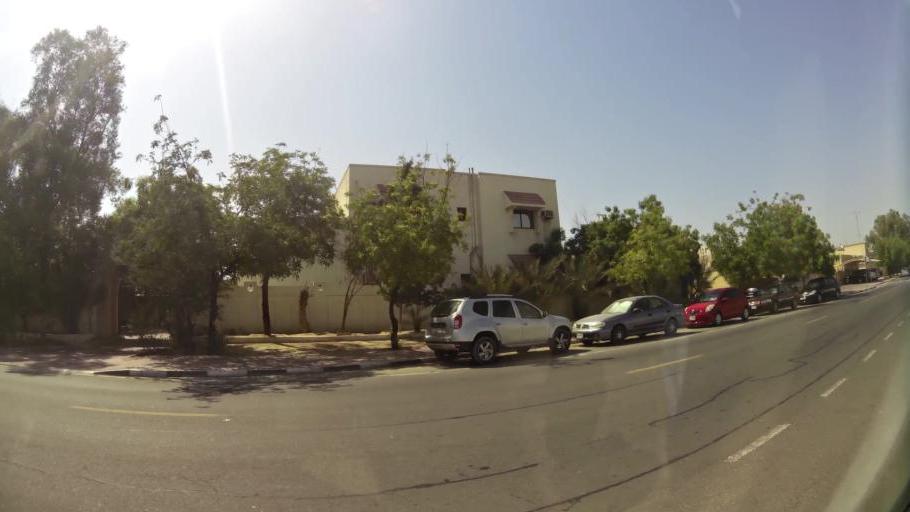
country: AE
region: Ash Shariqah
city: Sharjah
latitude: 25.2677
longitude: 55.3732
